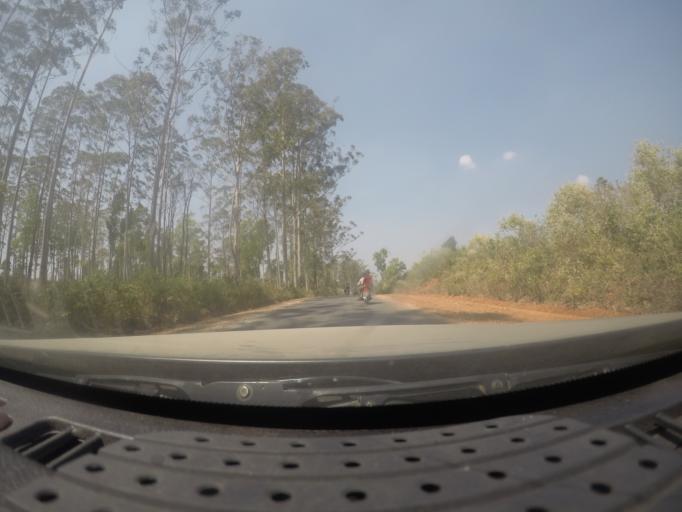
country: MM
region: Shan
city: Taunggyi
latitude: 20.9884
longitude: 96.5355
